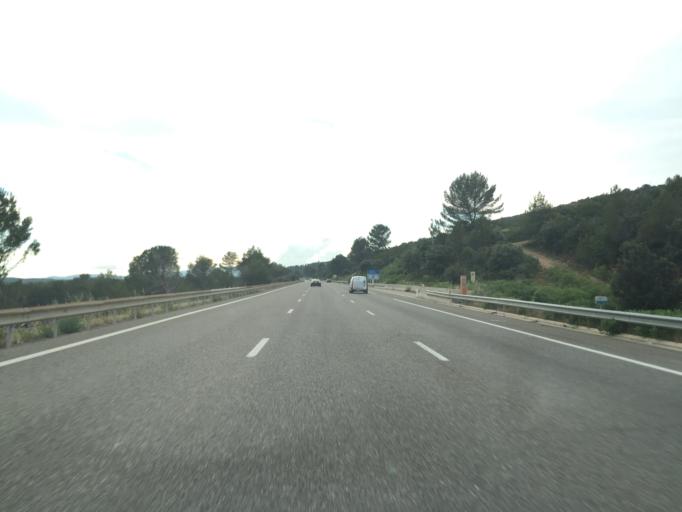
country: FR
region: Provence-Alpes-Cote d'Azur
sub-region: Departement du Var
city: La Celle
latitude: 43.4199
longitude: 6.0179
